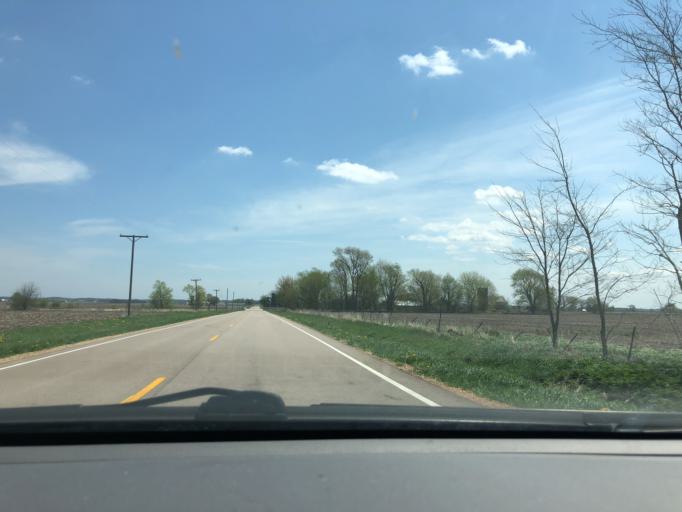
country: US
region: Illinois
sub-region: Kane County
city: Hampshire
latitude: 42.1100
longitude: -88.5782
